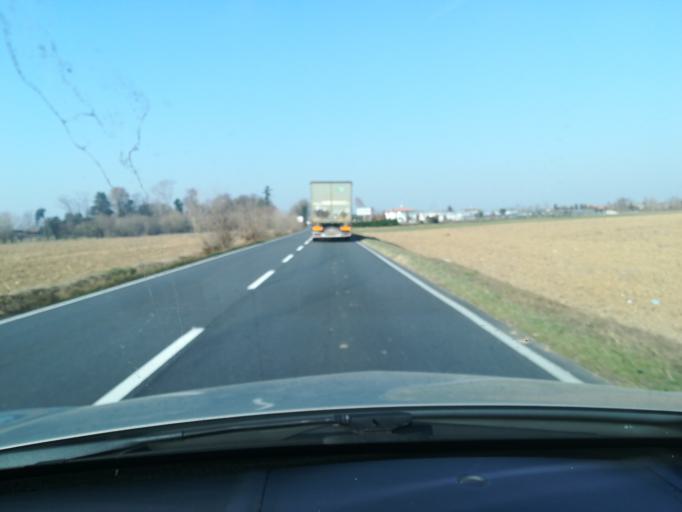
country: IT
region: Lombardy
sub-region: Provincia di Bergamo
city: Calcinate
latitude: 45.6070
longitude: 9.7996
